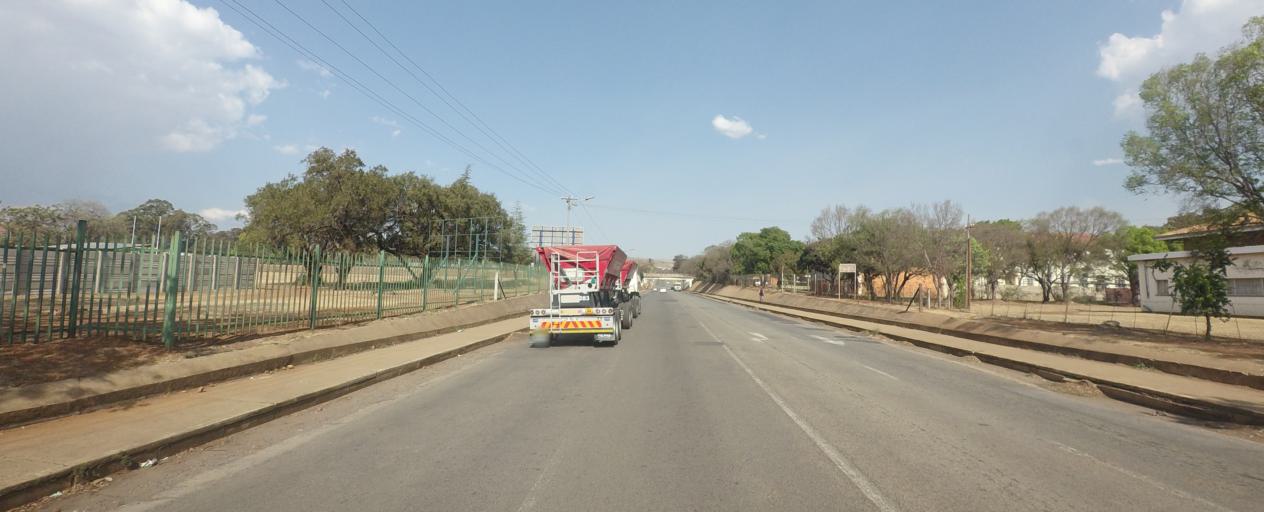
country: ZA
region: Mpumalanga
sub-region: Ehlanzeni District
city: Lydenburg
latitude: -25.0978
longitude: 30.4610
